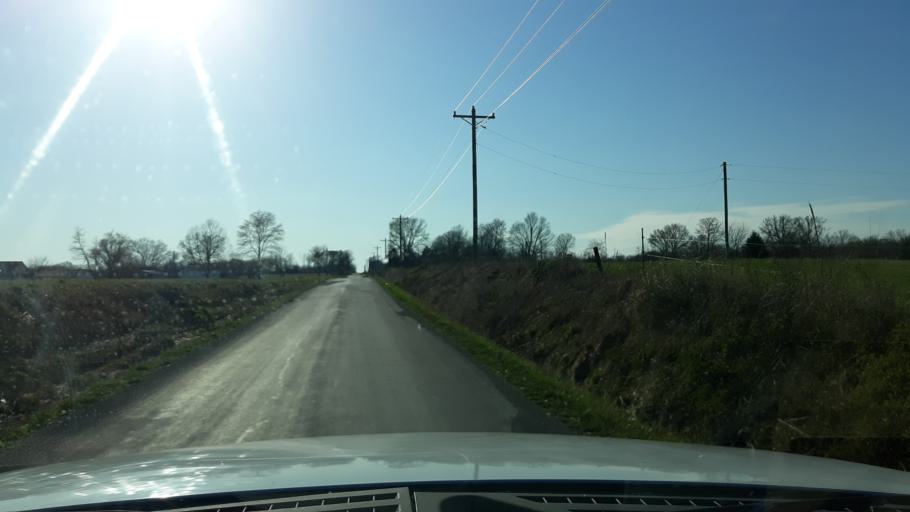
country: US
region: Illinois
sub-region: Saline County
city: Harrisburg
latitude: 37.8049
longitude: -88.6059
